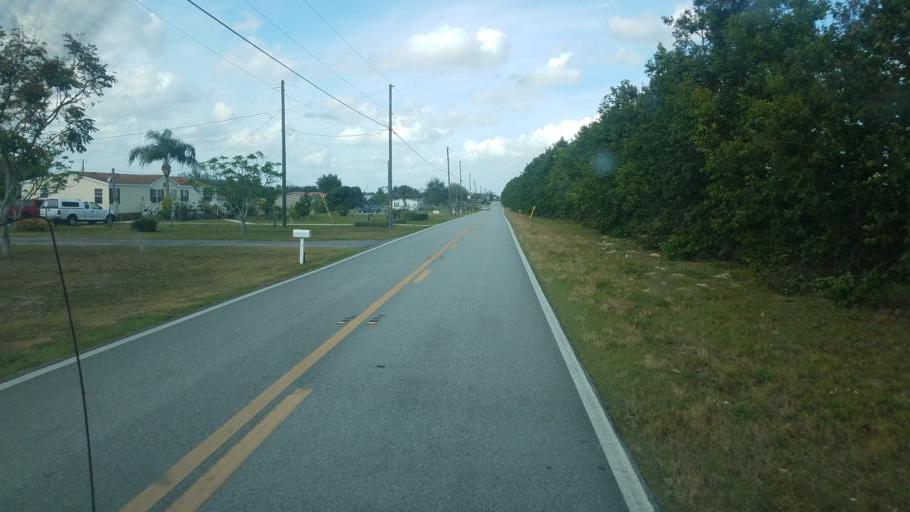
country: US
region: Florida
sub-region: Polk County
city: Lake Hamilton
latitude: 28.0718
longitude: -81.5789
